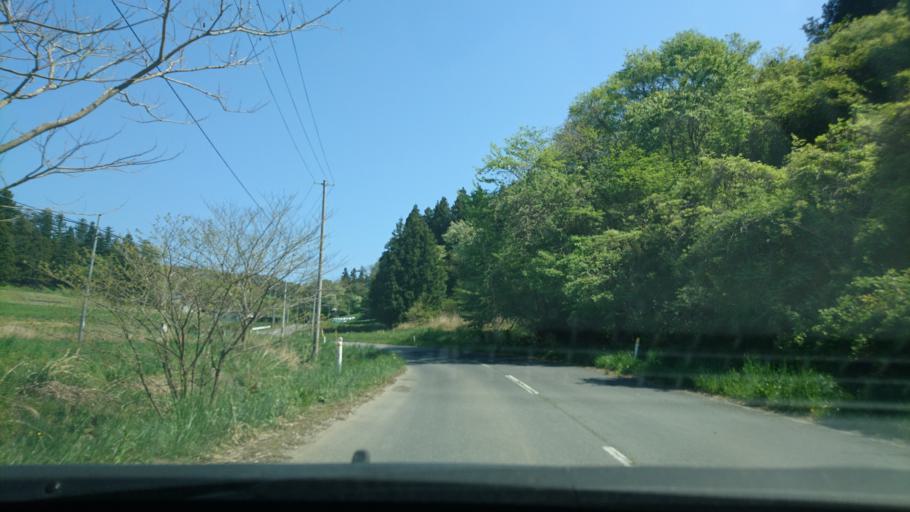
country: JP
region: Iwate
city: Ichinoseki
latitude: 38.9382
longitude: 141.2757
